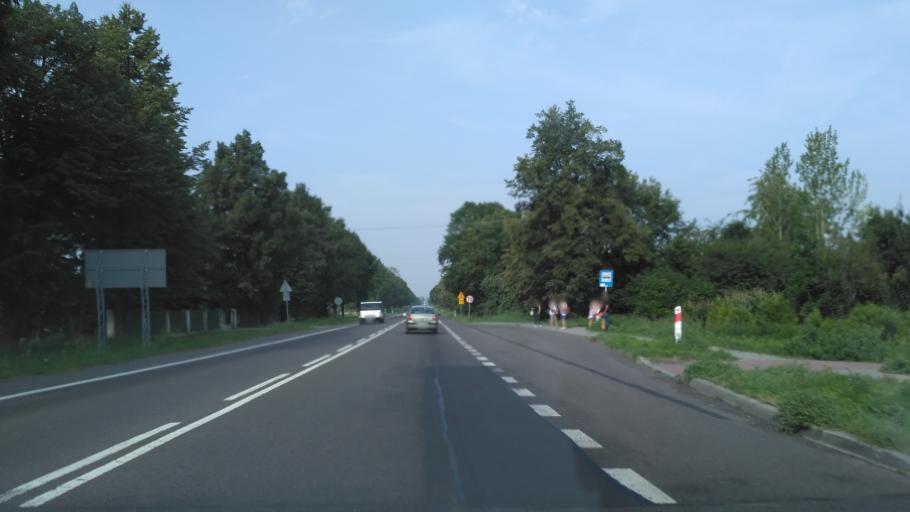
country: PL
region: Lublin Voivodeship
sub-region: Powiat swidnicki
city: Trawniki
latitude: 51.1596
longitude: 22.9415
